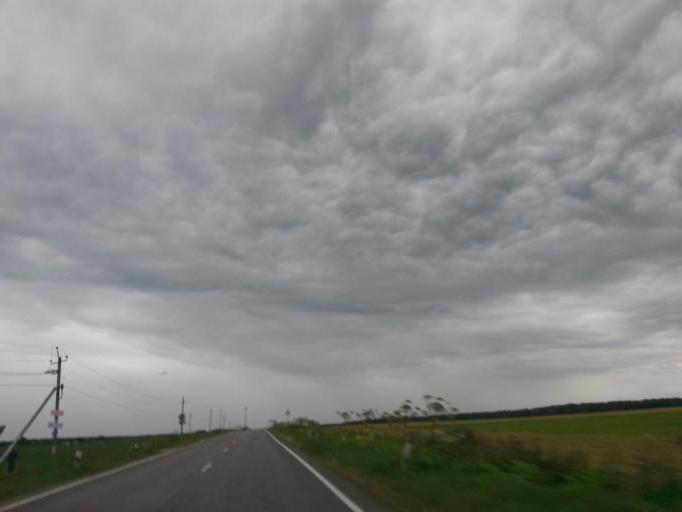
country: RU
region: Moskovskaya
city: Belyye Stolby
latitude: 55.2680
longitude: 37.7812
